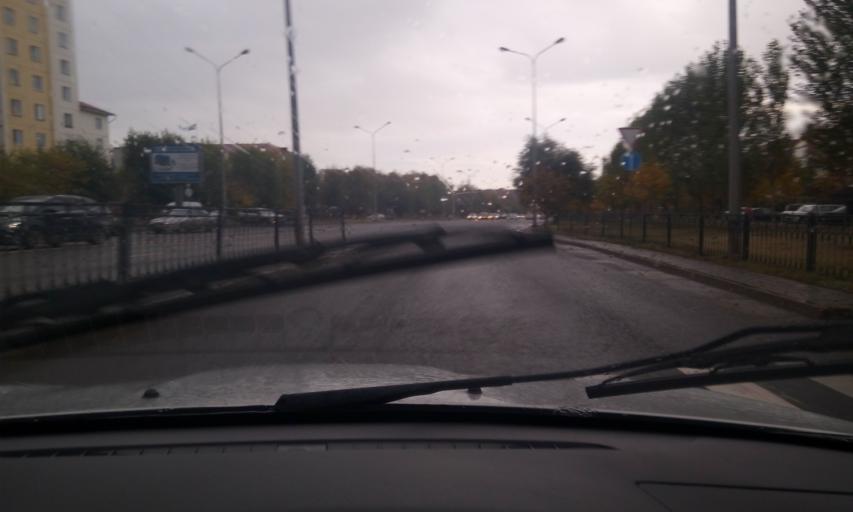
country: KZ
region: Astana Qalasy
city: Astana
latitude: 51.1563
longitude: 71.4775
